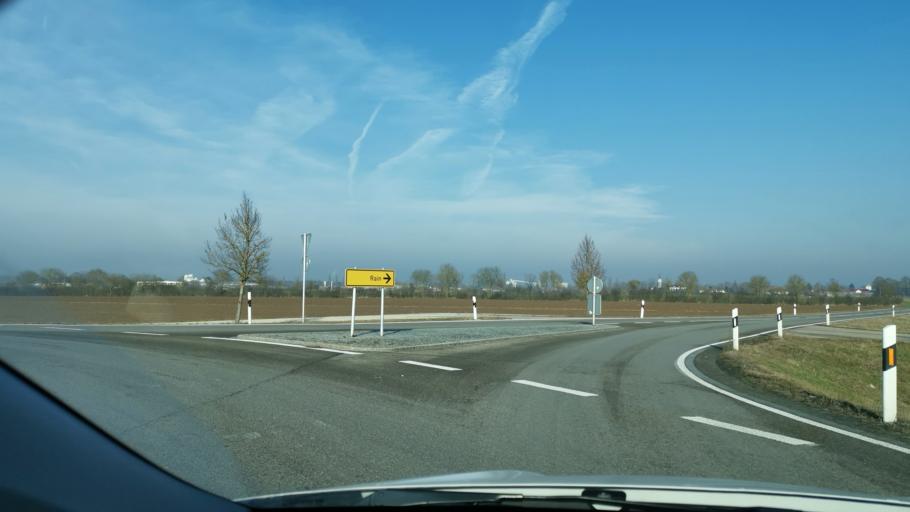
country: DE
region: Bavaria
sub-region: Swabia
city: Rain
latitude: 48.6741
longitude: 10.9199
